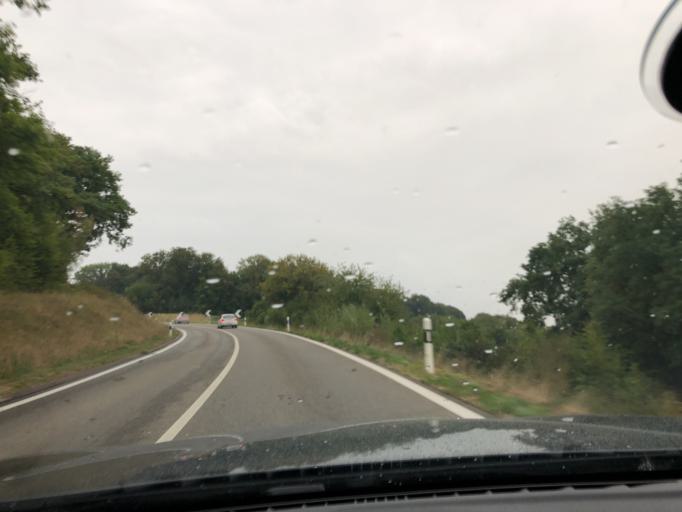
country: CH
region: Aargau
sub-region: Bezirk Bremgarten
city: Berikon
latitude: 47.3473
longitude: 8.3633
